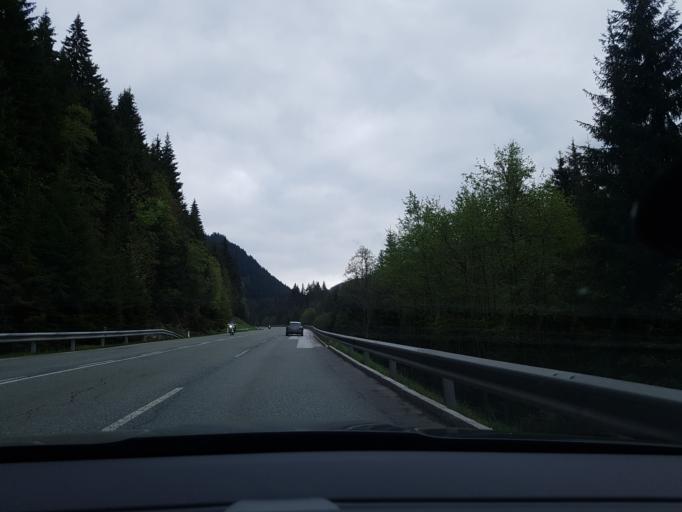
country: AT
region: Tyrol
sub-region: Politischer Bezirk Kitzbuhel
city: Jochberg
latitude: 47.3266
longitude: 12.4101
